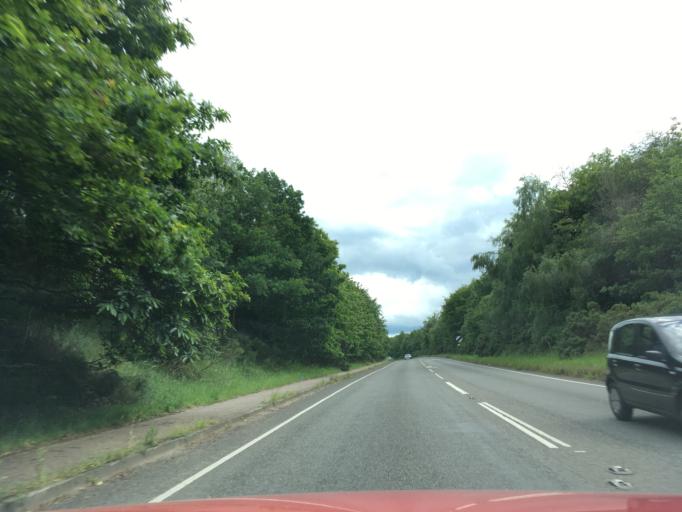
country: GB
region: England
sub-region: Milton Keynes
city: Woburn Sands
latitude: 52.0051
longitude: -0.6434
